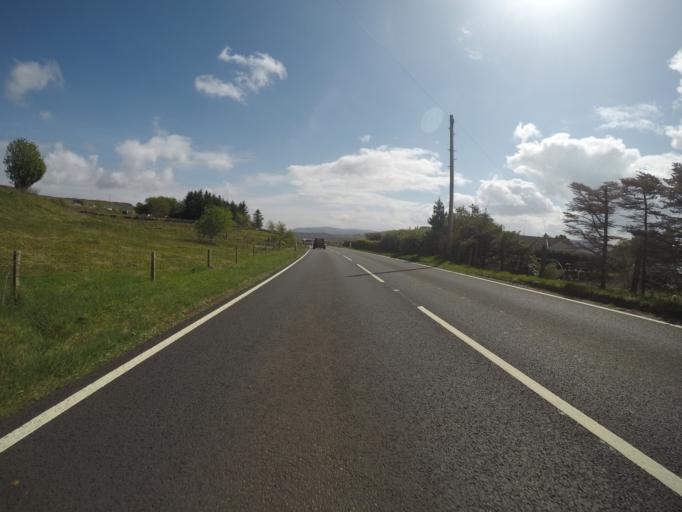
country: GB
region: Scotland
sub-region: Highland
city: Portree
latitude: 57.4930
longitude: -6.3194
